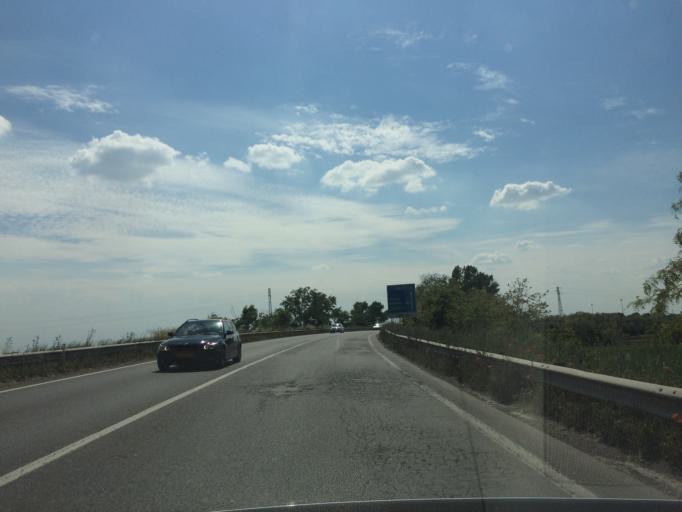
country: IT
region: Lombardy
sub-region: Provincia di Brescia
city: Rezzato
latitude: 45.4976
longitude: 10.3297
